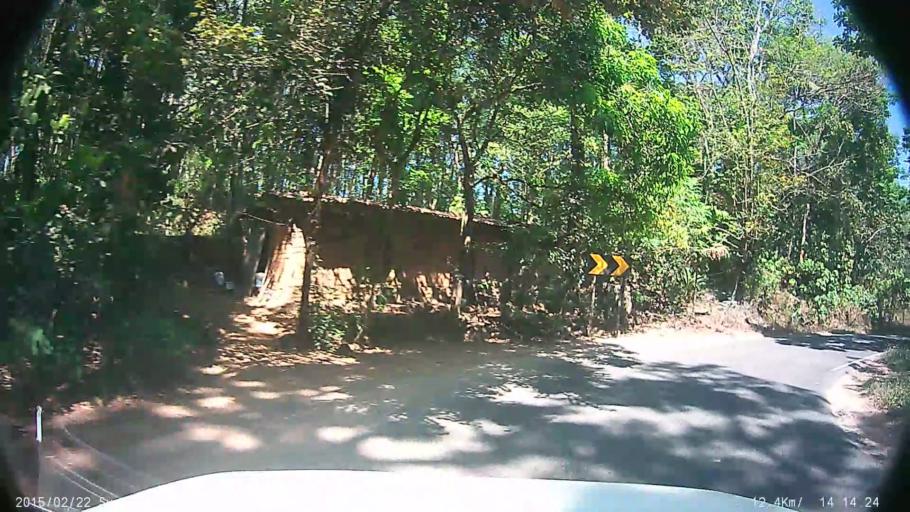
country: IN
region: Kerala
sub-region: Kottayam
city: Kottayam
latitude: 9.5439
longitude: 76.6839
